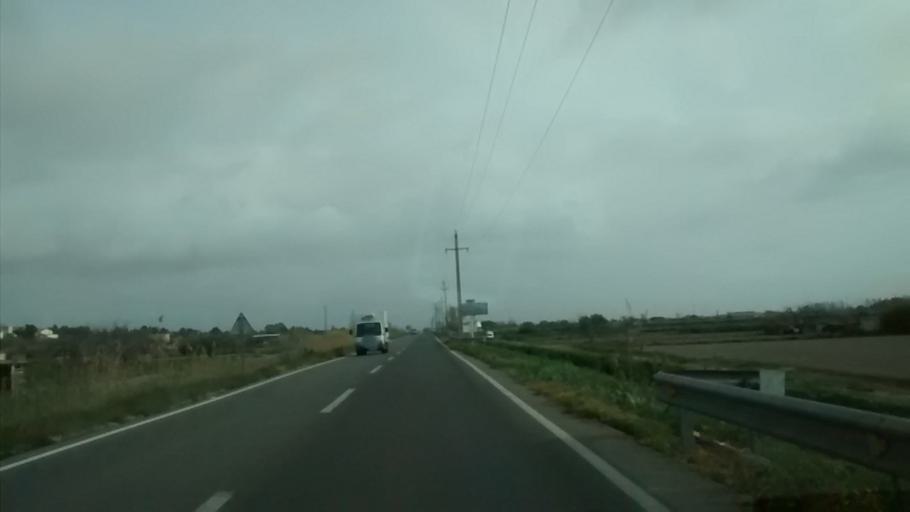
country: ES
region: Catalonia
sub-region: Provincia de Tarragona
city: Sant Carles de la Rapita
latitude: 40.6233
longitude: 0.5994
